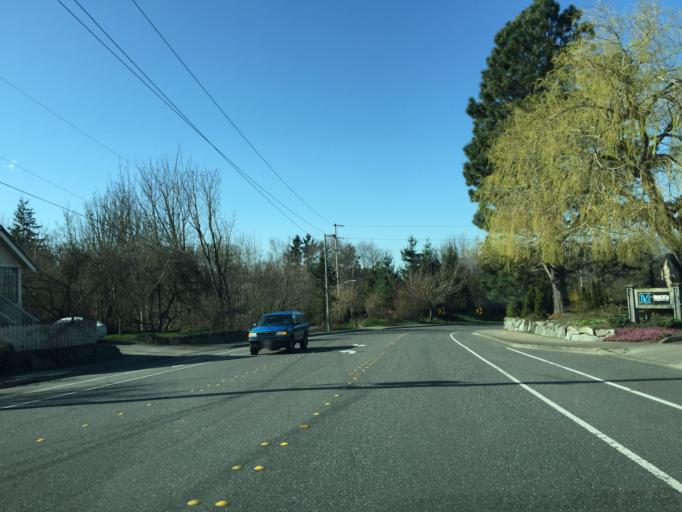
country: US
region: Washington
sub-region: Whatcom County
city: Bellingham
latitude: 48.7177
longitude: -122.5031
